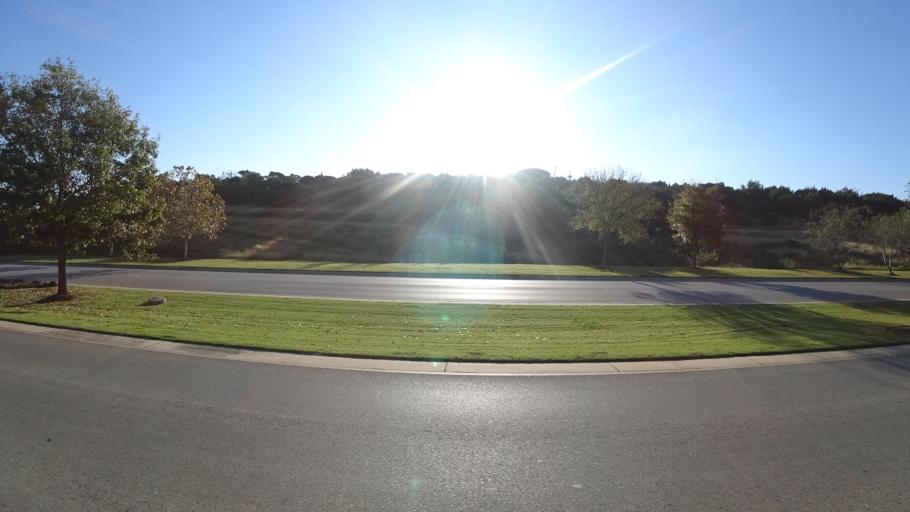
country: US
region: Texas
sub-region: Travis County
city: Hudson Bend
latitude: 30.3729
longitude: -97.8868
